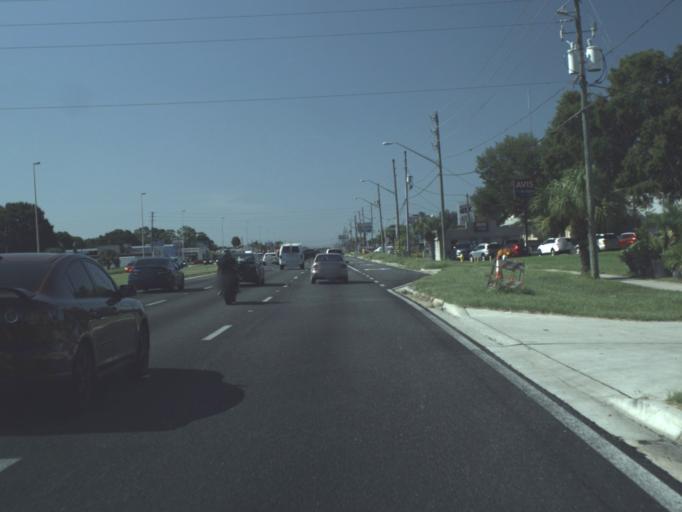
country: US
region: Florida
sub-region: Pasco County
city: Port Richey
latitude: 28.2644
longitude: -82.7280
